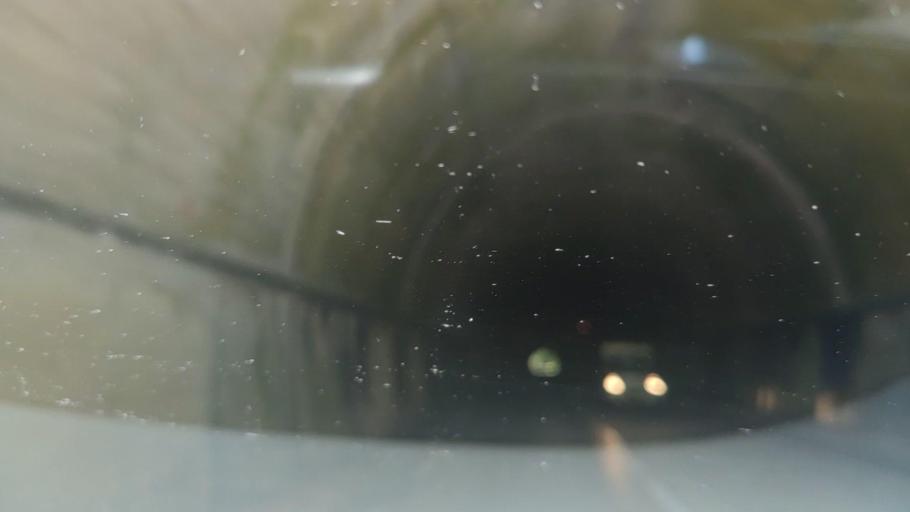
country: JP
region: Hyogo
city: Toyooka
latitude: 35.6372
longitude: 134.7784
